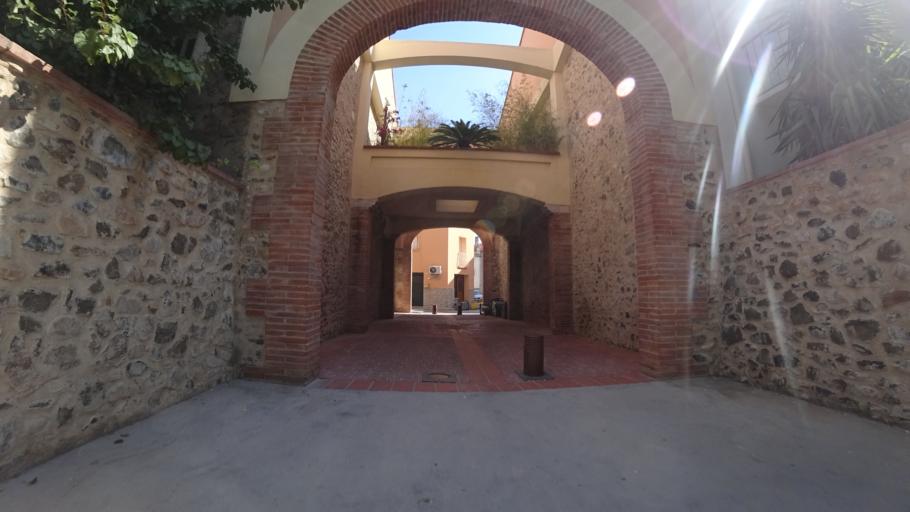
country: FR
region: Languedoc-Roussillon
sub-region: Departement des Pyrenees-Orientales
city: Peyrestortes
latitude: 42.7770
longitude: 2.8368
